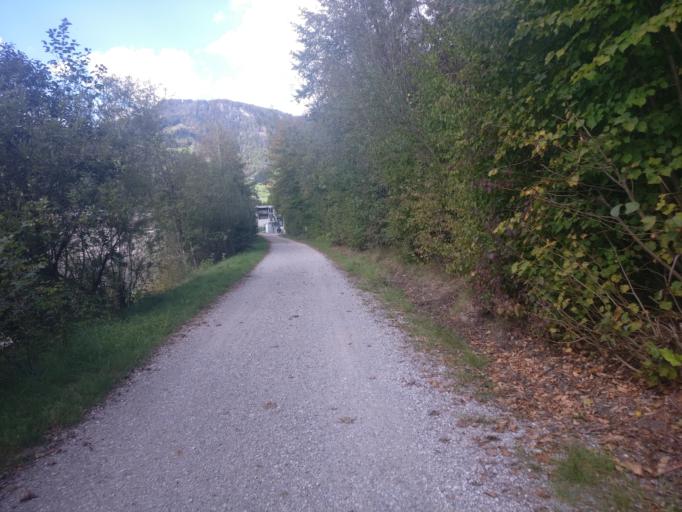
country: AT
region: Salzburg
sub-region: Politischer Bezirk Sankt Johann im Pongau
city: Bischofshofen
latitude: 47.4062
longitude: 13.2221
